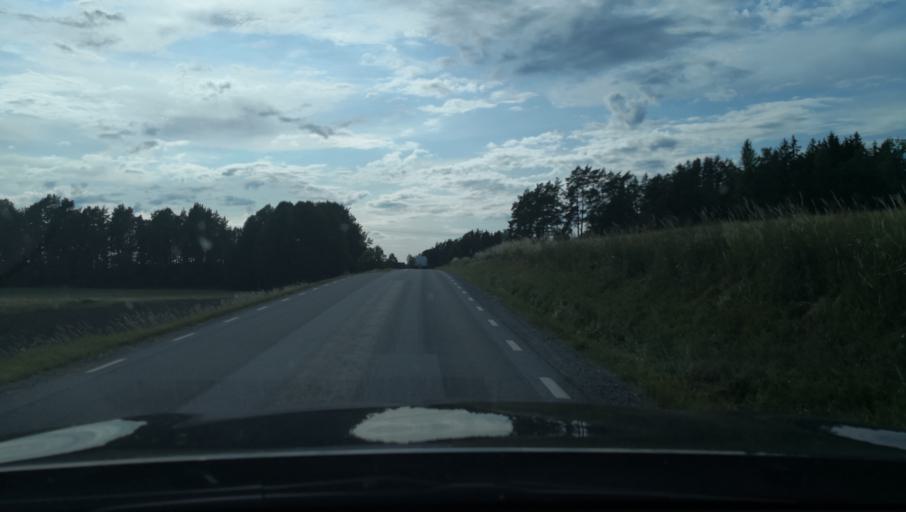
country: SE
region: Uppsala
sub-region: Enkopings Kommun
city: Orsundsbro
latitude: 59.6749
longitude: 17.4236
